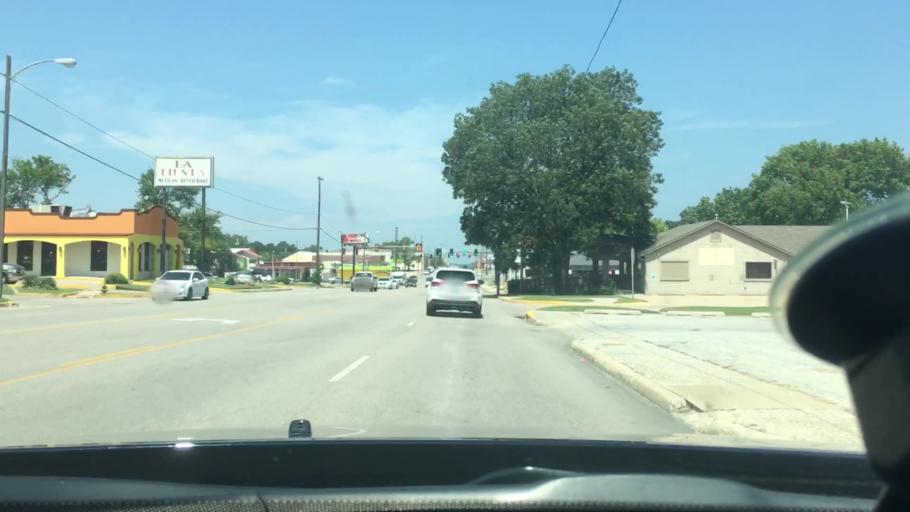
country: US
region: Oklahoma
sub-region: Pontotoc County
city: Ada
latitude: 34.7719
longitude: -96.6698
